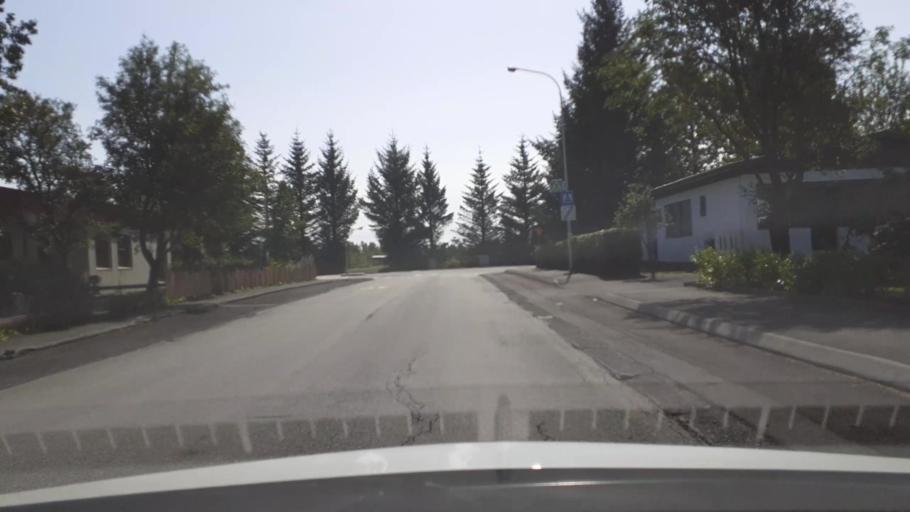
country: IS
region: South
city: Selfoss
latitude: 63.9343
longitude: -20.9871
